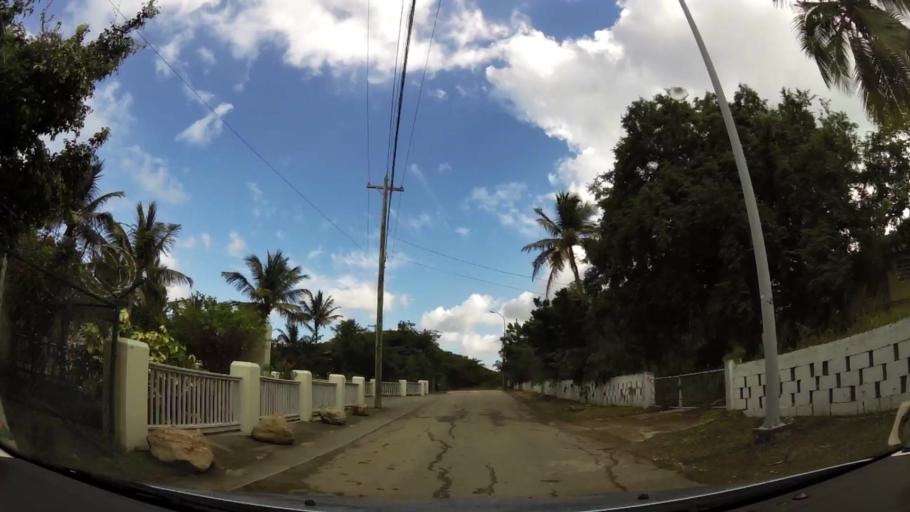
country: AG
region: Saint John
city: Saint John's
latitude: 17.1182
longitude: -61.8920
